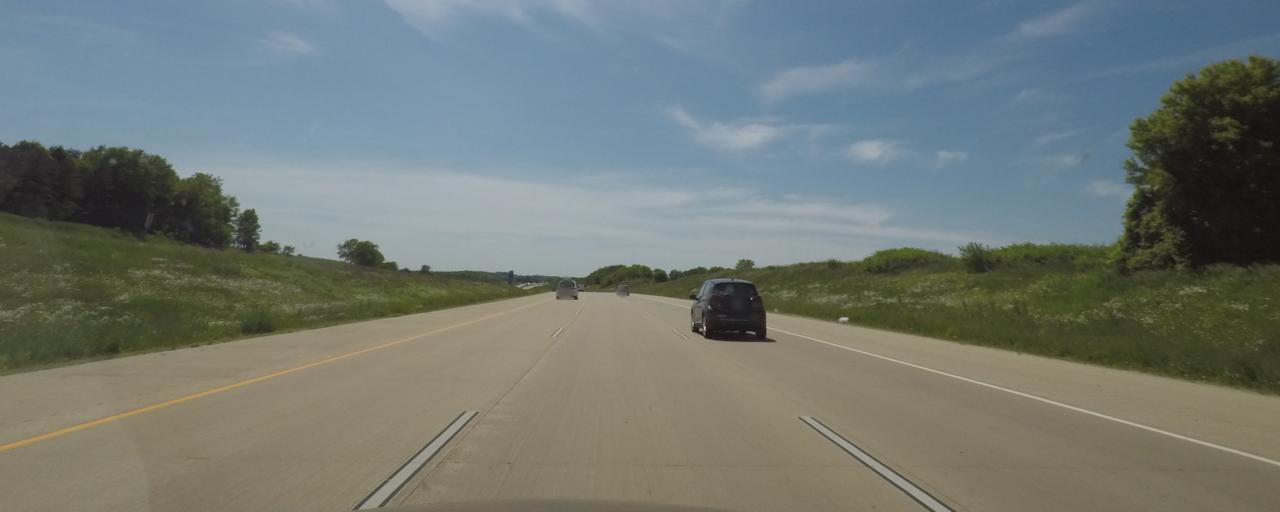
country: US
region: Wisconsin
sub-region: Dane County
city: Cottage Grove
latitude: 43.1082
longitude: -89.2303
